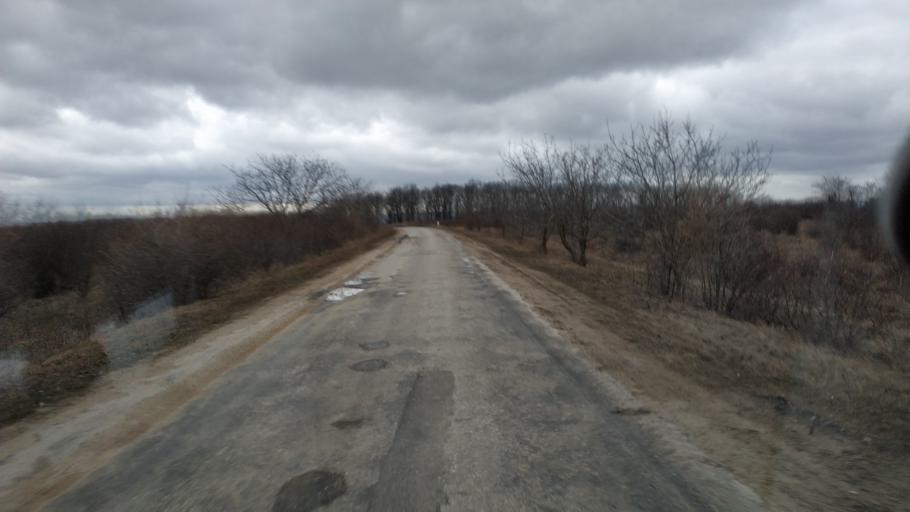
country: MD
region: Calarasi
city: Calarasi
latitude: 47.2263
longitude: 28.2529
